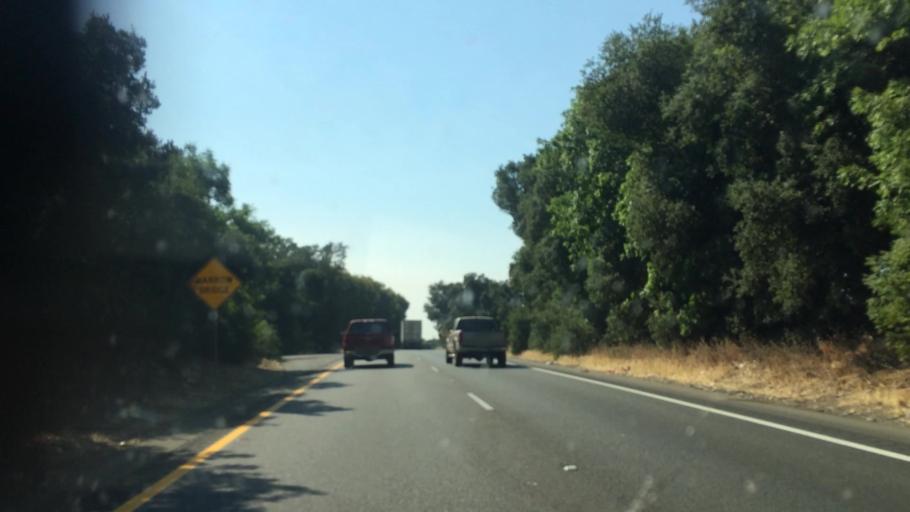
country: US
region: California
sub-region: Sacramento County
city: Elk Grove
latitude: 38.3606
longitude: -121.3461
